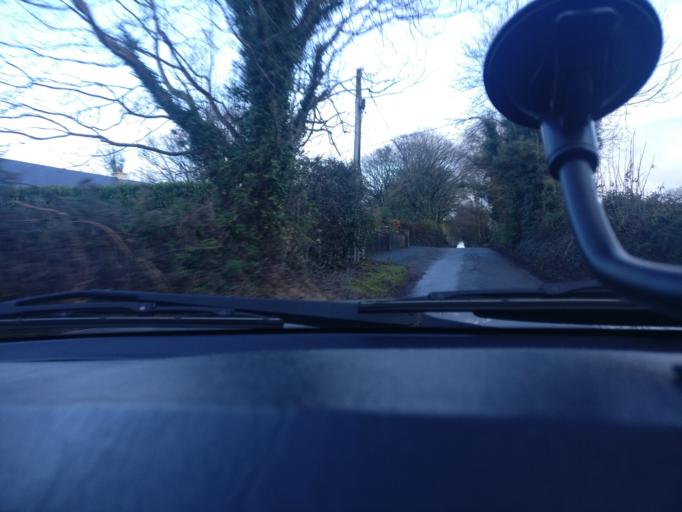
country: IE
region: Connaught
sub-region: County Galway
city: Athenry
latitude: 53.1986
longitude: -8.7028
